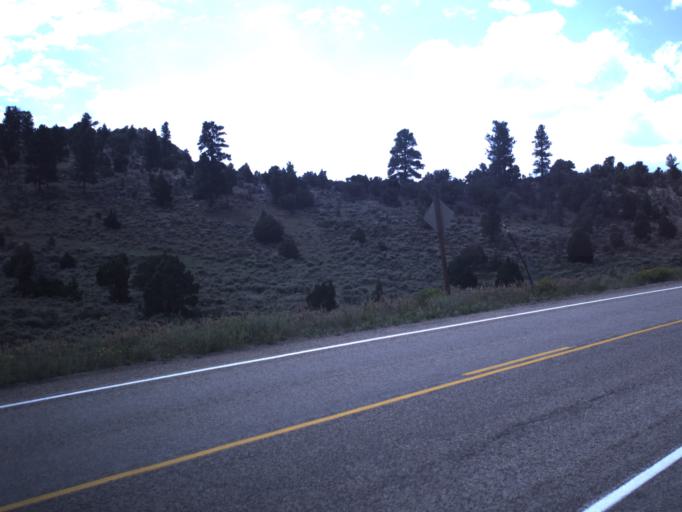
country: US
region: Utah
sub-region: Daggett County
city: Manila
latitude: 40.8991
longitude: -109.7043
